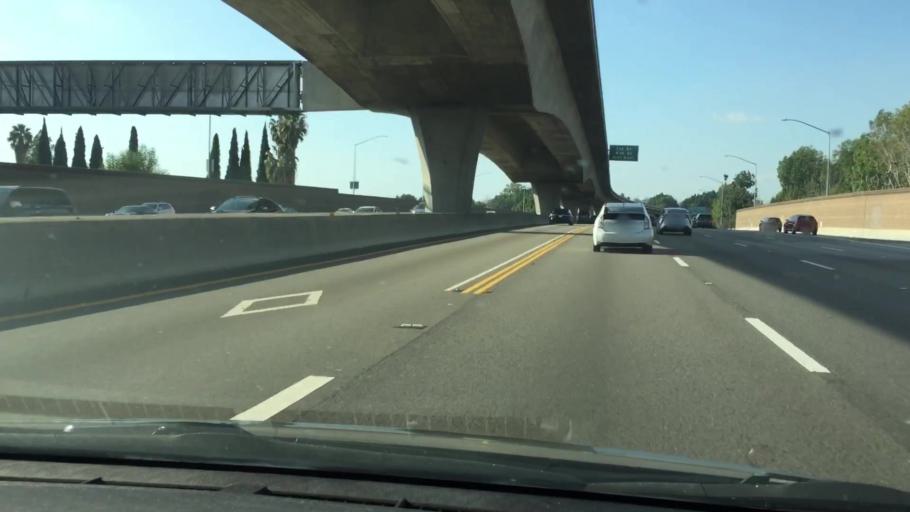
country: US
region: California
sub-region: Orange County
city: Tustin
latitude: 33.7419
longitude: -117.8371
